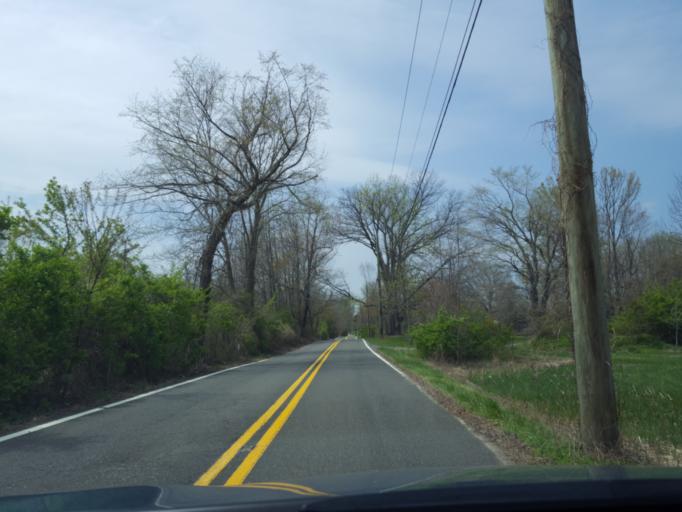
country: US
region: Maryland
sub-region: Prince George's County
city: Croom
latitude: 38.7412
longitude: -76.7265
